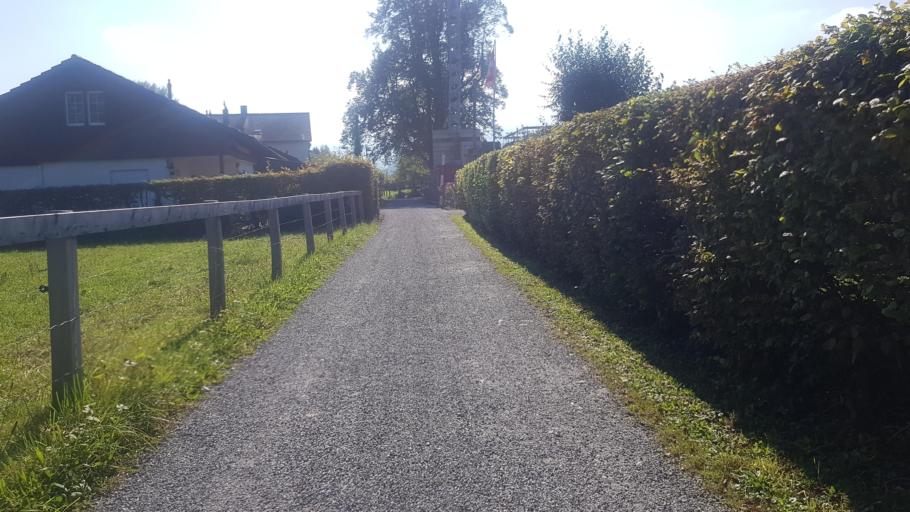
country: CH
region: Saint Gallen
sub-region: Wahlkreis Rheintal
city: Rheineck
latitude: 47.4932
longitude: 9.5636
